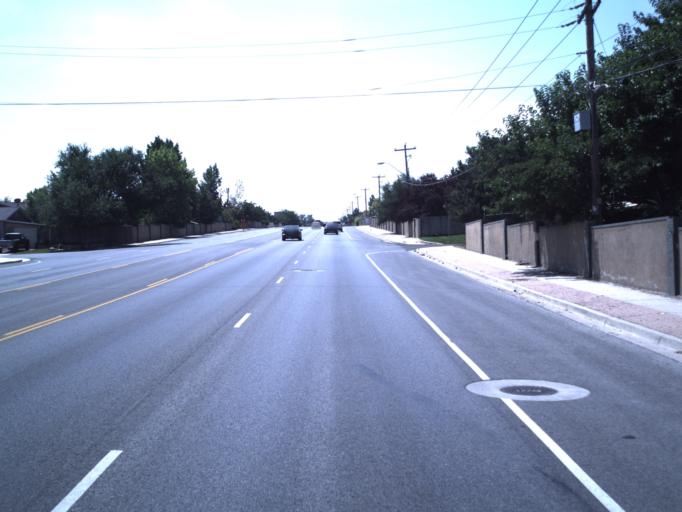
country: US
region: Utah
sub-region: Salt Lake County
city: West Valley City
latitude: 40.6766
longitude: -112.0248
